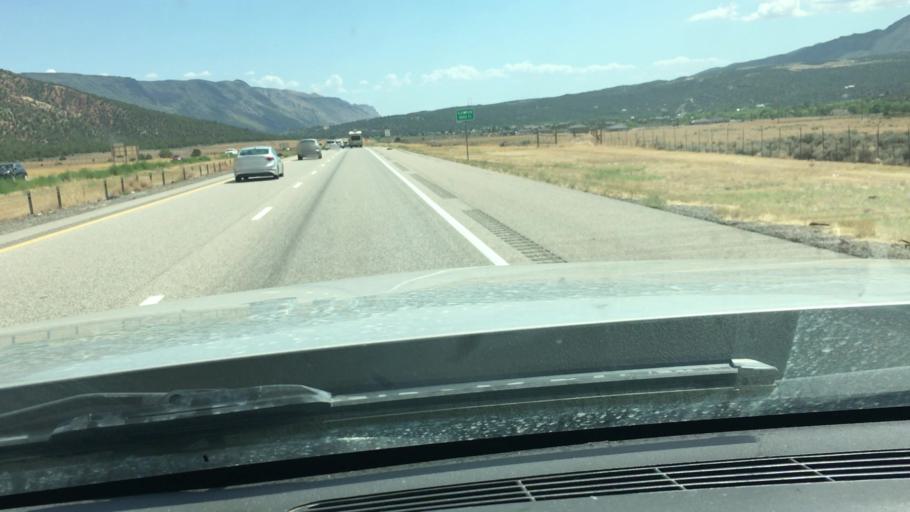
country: US
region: Utah
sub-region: Washington County
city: Toquerville
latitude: 37.4460
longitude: -113.2306
